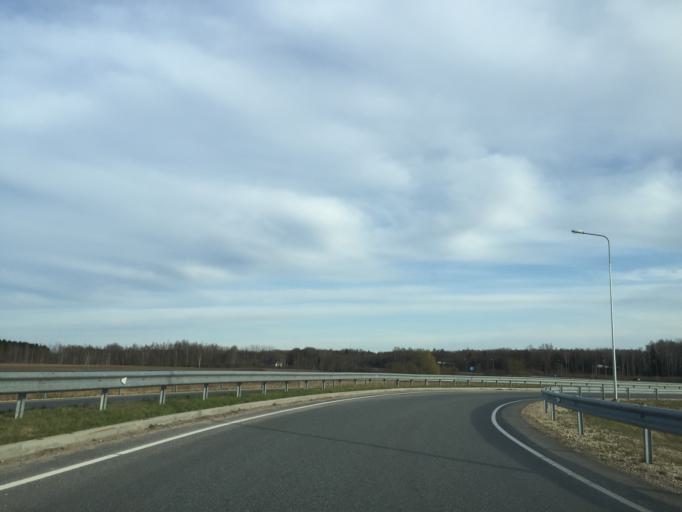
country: LV
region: Lielvarde
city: Lielvarde
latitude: 56.8083
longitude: 24.8852
